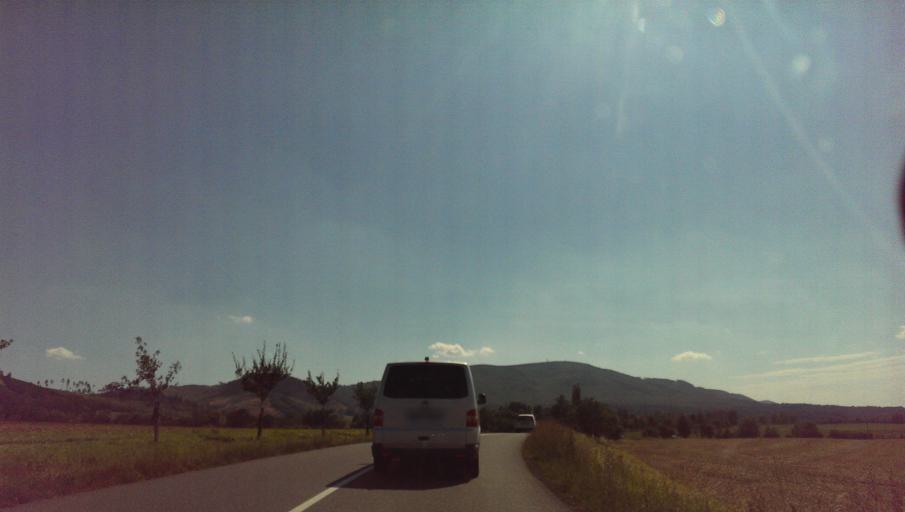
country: CZ
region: Zlin
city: Kelc
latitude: 49.4364
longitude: 17.8034
